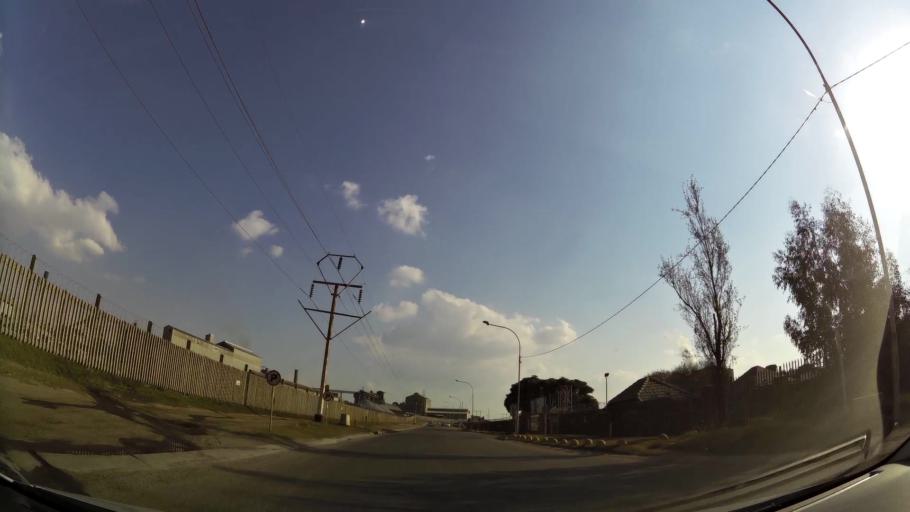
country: ZA
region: Gauteng
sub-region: Ekurhuleni Metropolitan Municipality
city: Tembisa
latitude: -25.9445
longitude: 28.2287
